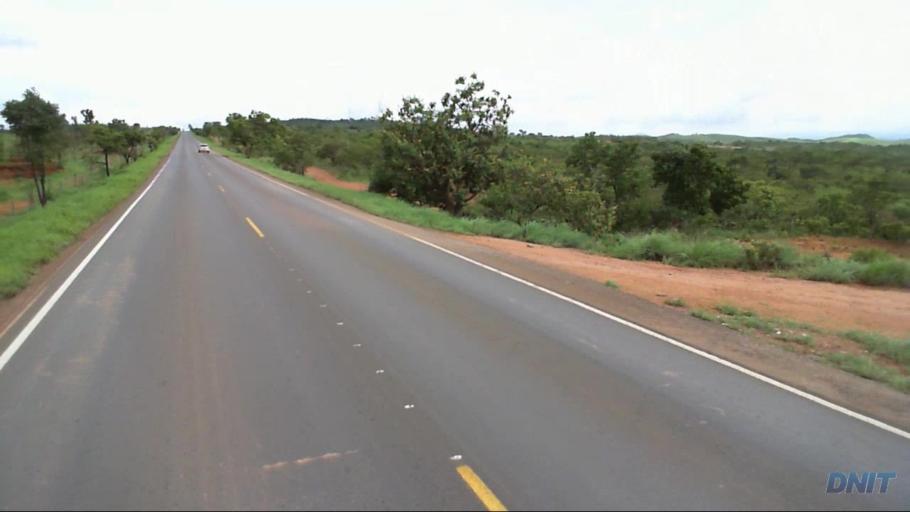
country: BR
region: Goias
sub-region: Padre Bernardo
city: Padre Bernardo
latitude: -15.2344
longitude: -48.2748
